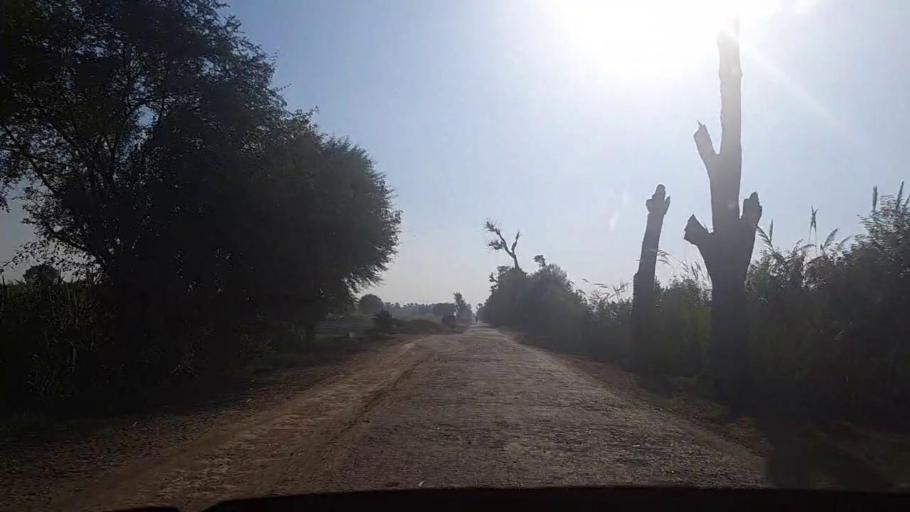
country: PK
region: Sindh
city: Gambat
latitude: 27.3608
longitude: 68.4576
